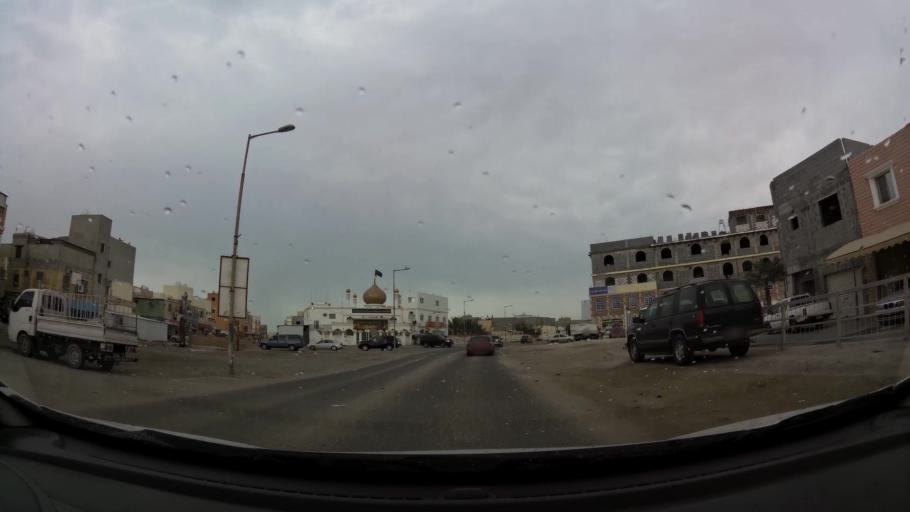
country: BH
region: Central Governorate
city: Madinat Hamad
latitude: 26.1270
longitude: 50.4775
